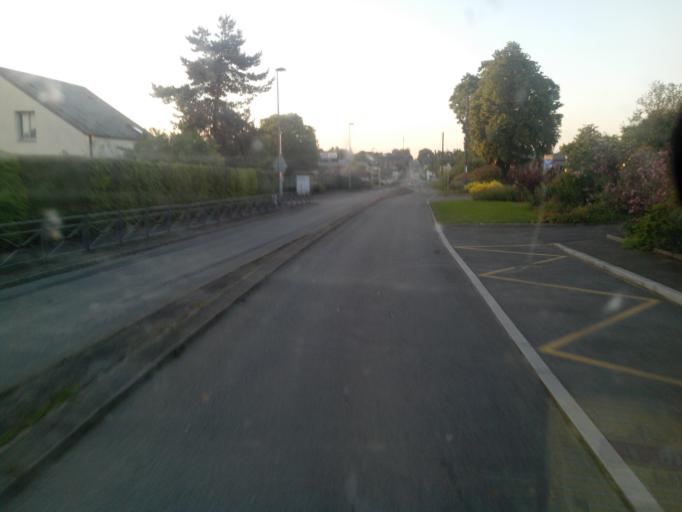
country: FR
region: Brittany
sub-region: Departement d'Ille-et-Vilaine
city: Lecousse
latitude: 48.3655
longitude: -1.2090
